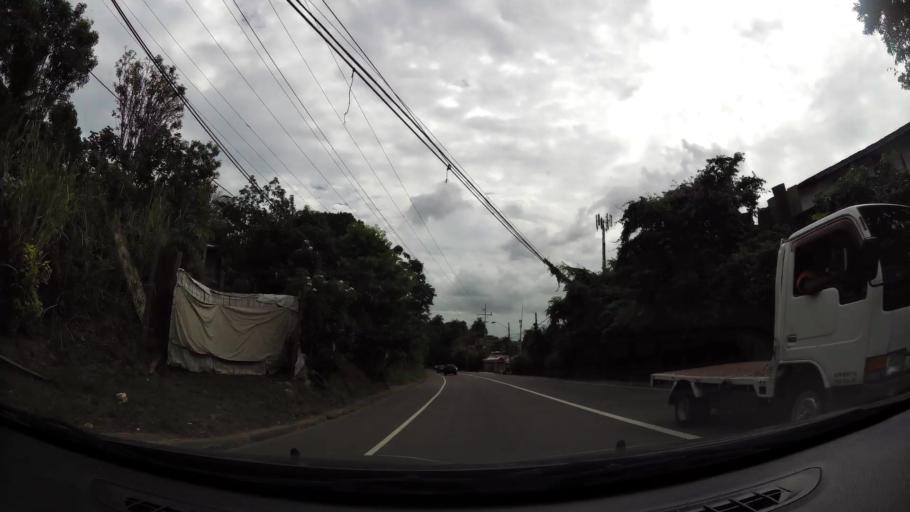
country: TT
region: San Juan/Laventille
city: Laventille
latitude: 10.6669
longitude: -61.4833
